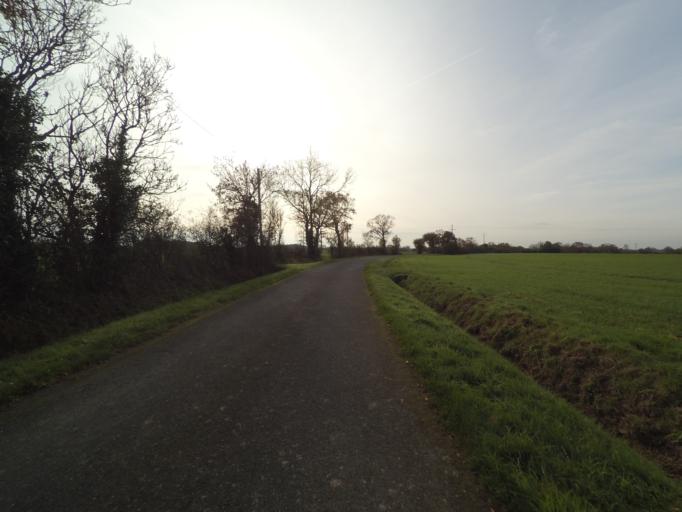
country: FR
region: Pays de la Loire
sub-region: Departement de la Loire-Atlantique
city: La Planche
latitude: 46.9990
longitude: -1.3962
